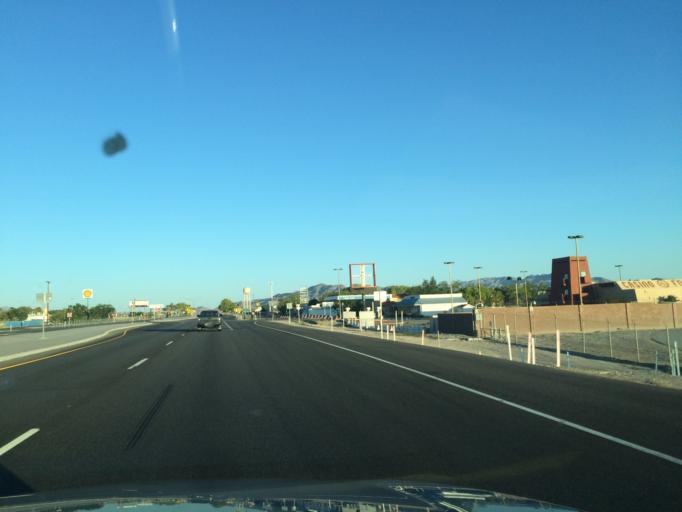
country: US
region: Nevada
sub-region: Nye County
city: Pahrump
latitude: 36.5779
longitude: -115.6658
